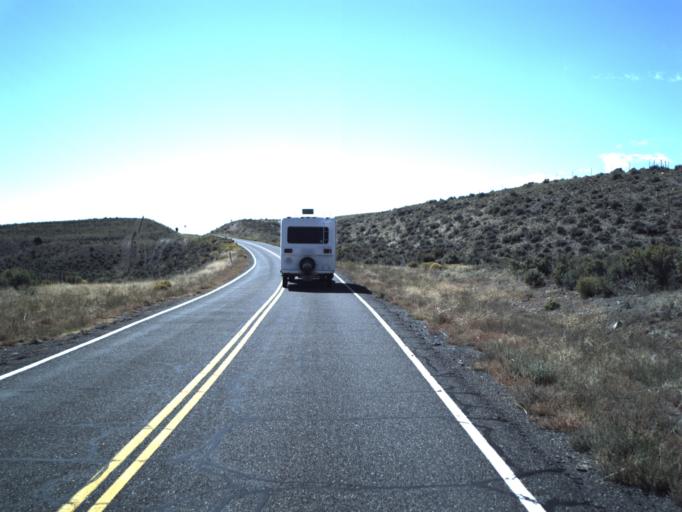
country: US
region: Utah
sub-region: Piute County
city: Junction
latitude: 38.3481
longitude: -111.9516
